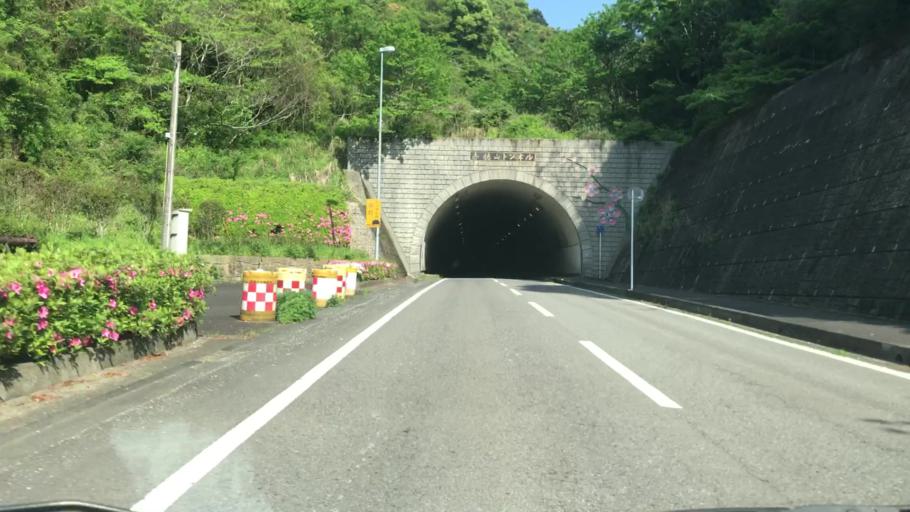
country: JP
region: Saga Prefecture
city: Takeocho-takeo
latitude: 33.2136
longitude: 130.0069
